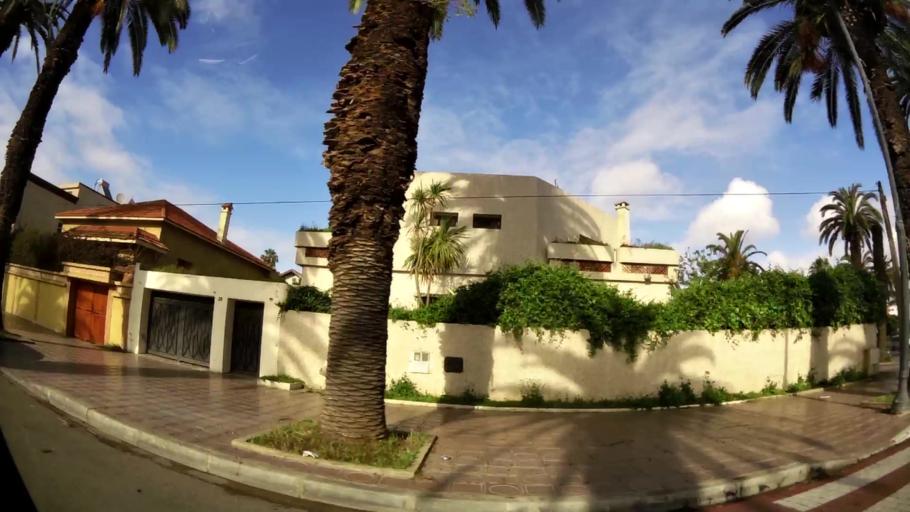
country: MA
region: Grand Casablanca
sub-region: Mohammedia
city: Mohammedia
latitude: 33.6987
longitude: -7.3928
